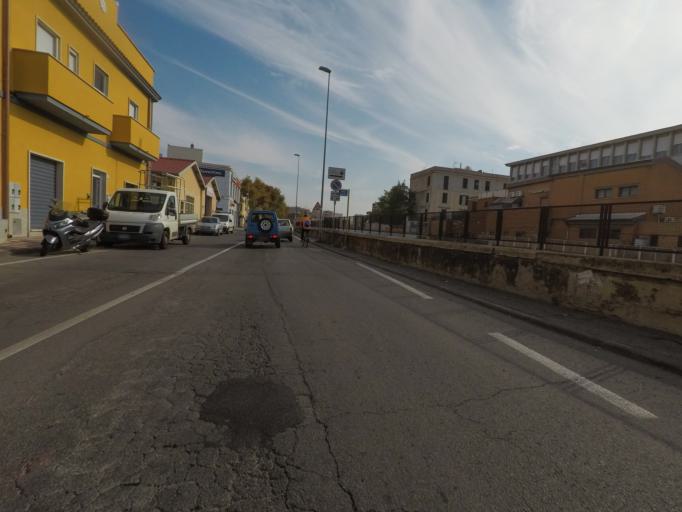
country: IT
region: Latium
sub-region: Citta metropolitana di Roma Capitale
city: Civitavecchia
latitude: 42.0957
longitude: 11.7942
